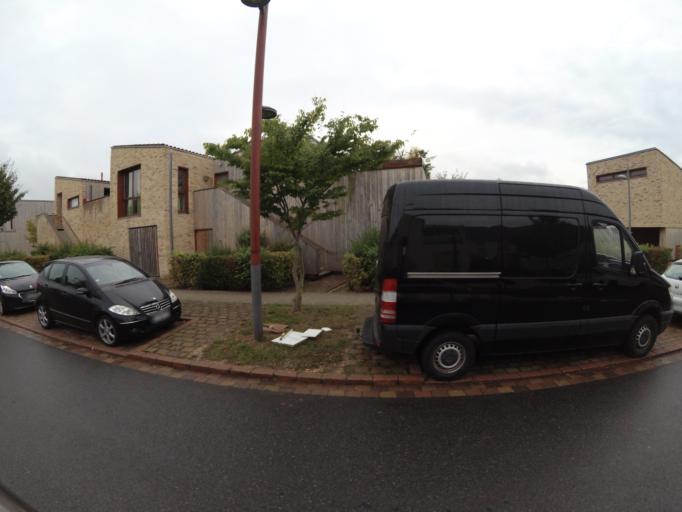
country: FR
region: Ile-de-France
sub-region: Departement de Seine-et-Marne
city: Chanteloup-en-Brie
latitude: 48.8573
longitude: 2.7453
